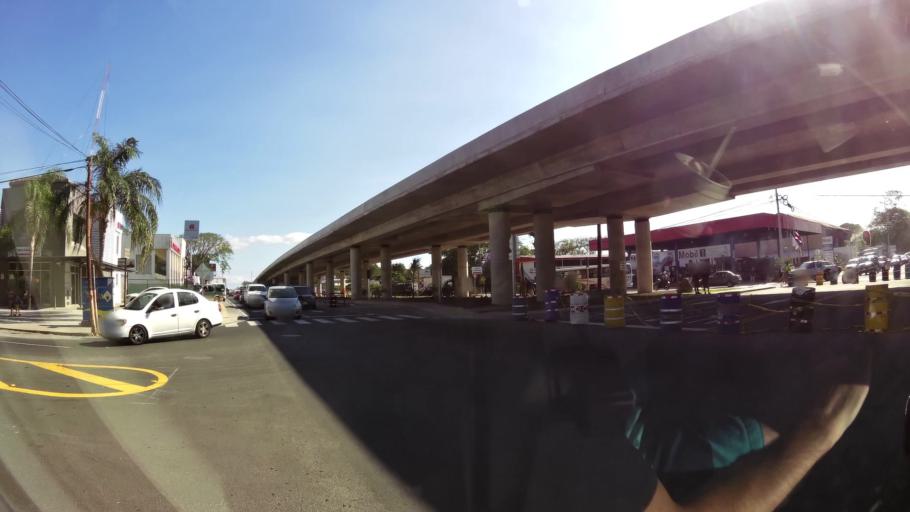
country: CR
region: Guanacaste
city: Liberia
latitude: 10.6269
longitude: -85.4436
